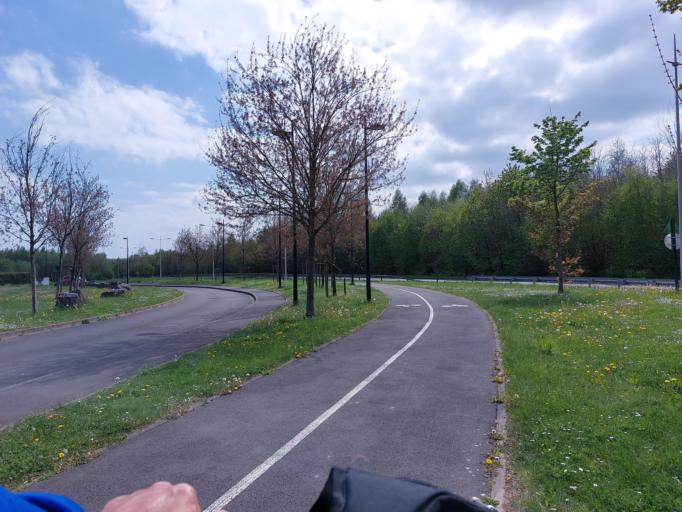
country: FR
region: Nord-Pas-de-Calais
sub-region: Departement du Nord
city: Hautmont
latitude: 50.2557
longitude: 3.8973
